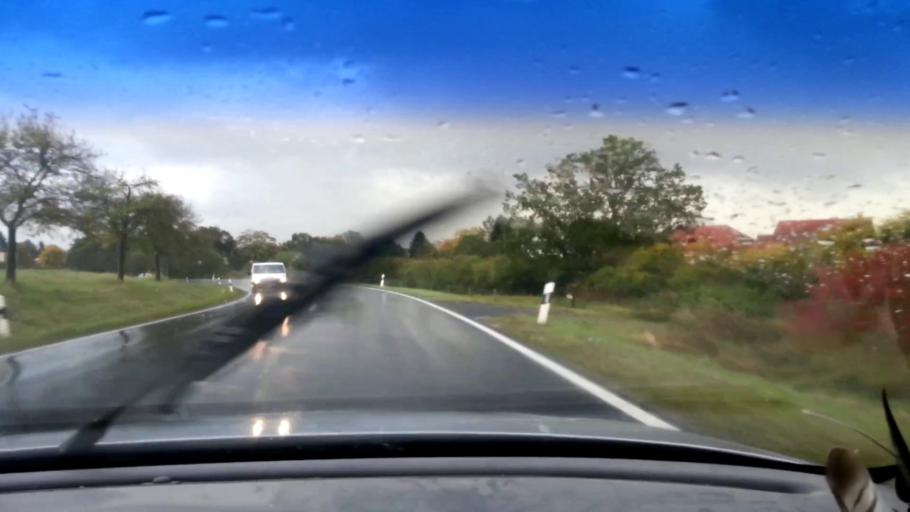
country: DE
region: Bavaria
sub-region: Upper Franconia
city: Burgebrach
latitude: 49.8357
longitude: 10.7387
